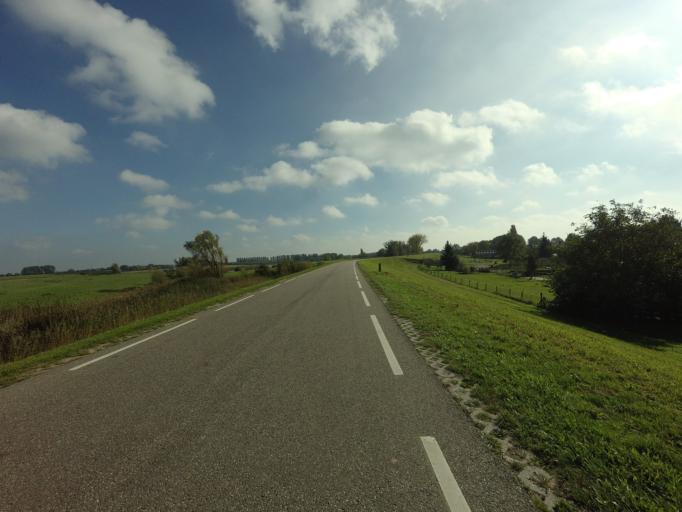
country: NL
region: Gelderland
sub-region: Gemeente Culemborg
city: Culemborg
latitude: 51.9630
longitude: 5.2642
